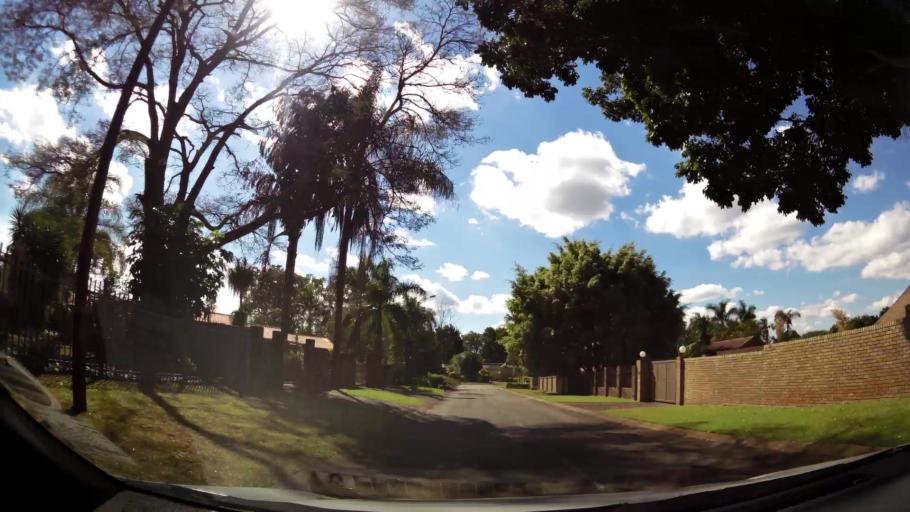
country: ZA
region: Limpopo
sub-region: Mopani District Municipality
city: Tzaneen
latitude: -23.8188
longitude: 30.1462
